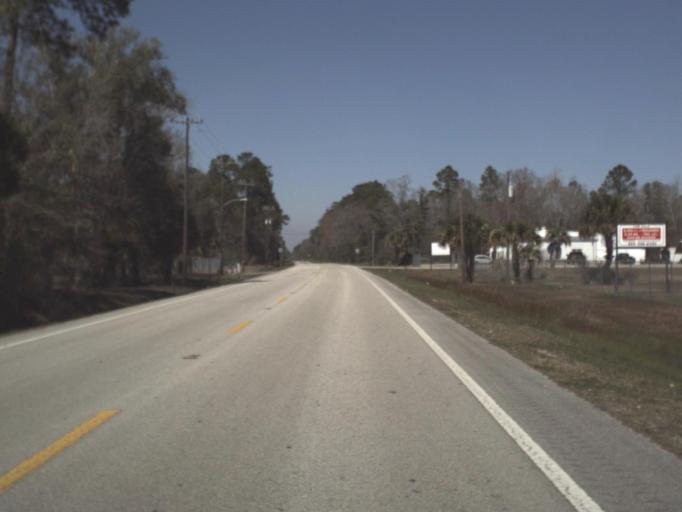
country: US
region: Florida
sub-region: Leon County
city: Woodville
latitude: 30.1694
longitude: -84.2085
